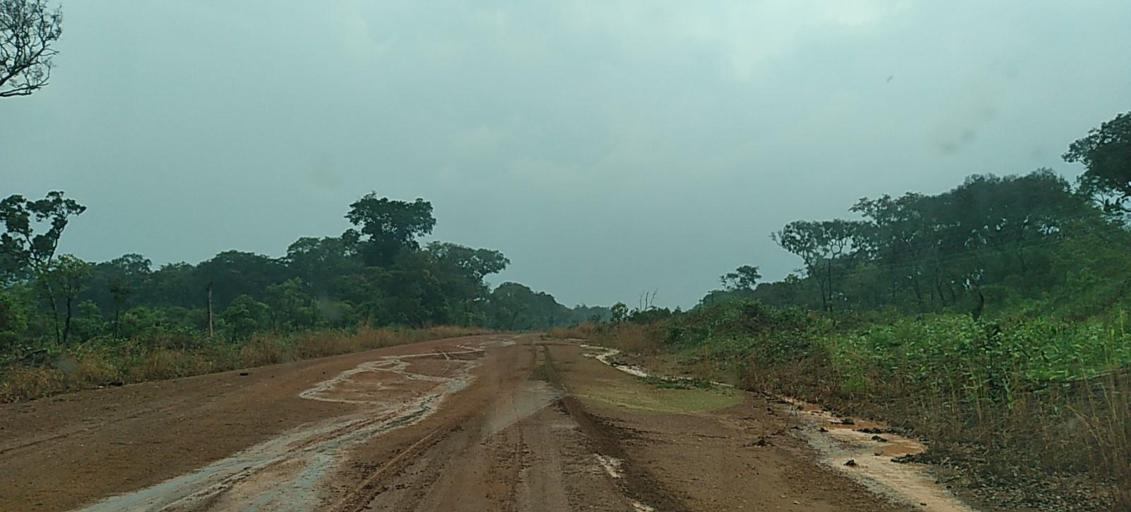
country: ZM
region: North-Western
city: Mwinilunga
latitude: -11.5981
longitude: 24.3921
